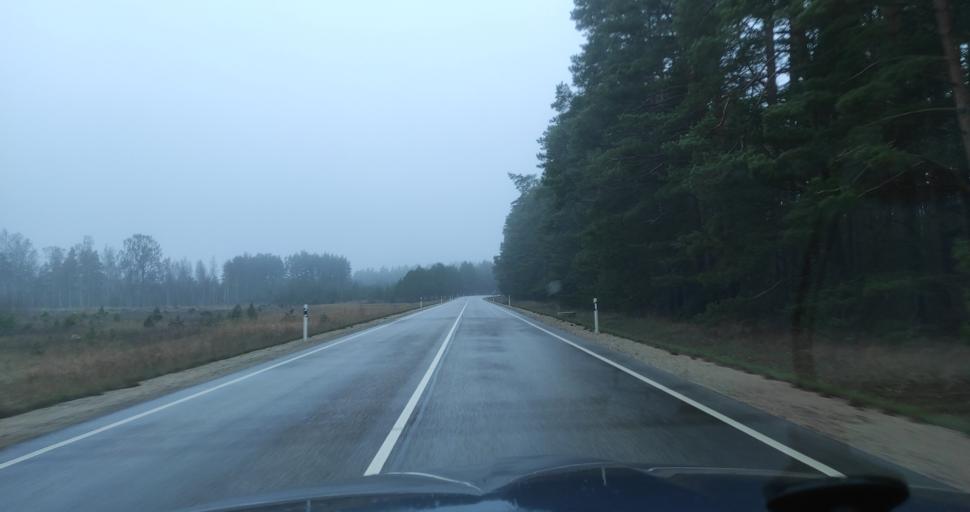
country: LV
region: Pavilostas
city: Pavilosta
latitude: 56.9488
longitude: 21.3007
